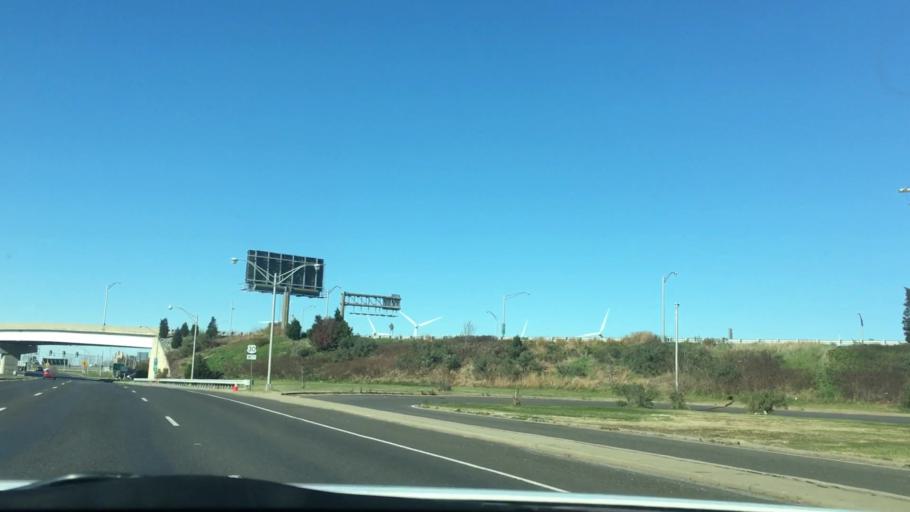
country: US
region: New Jersey
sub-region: Atlantic County
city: Atlantic City
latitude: 39.3729
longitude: -74.4372
